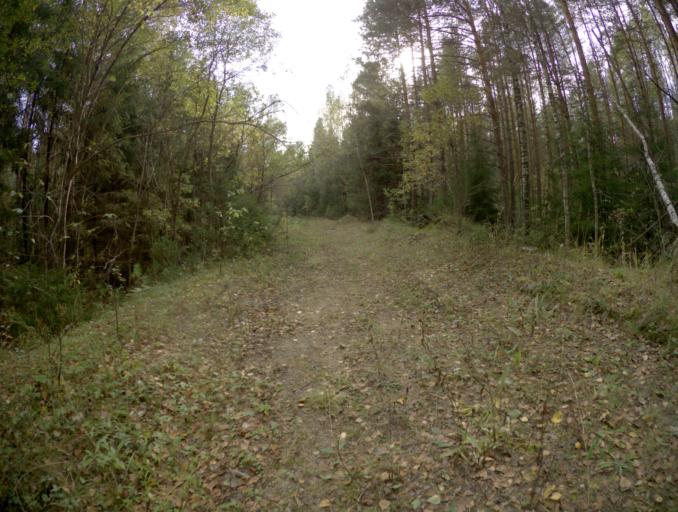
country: RU
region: Vladimir
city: Raduzhnyy
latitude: 55.9804
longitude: 40.2632
